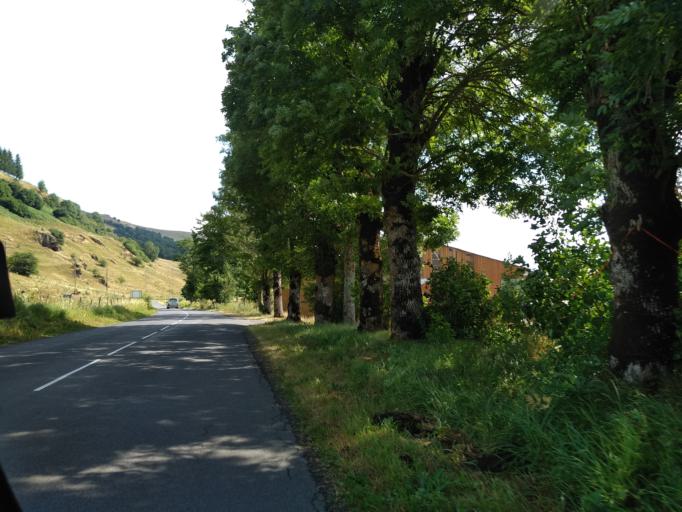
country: FR
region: Auvergne
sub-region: Departement du Cantal
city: Murat
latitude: 45.1516
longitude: 2.7766
